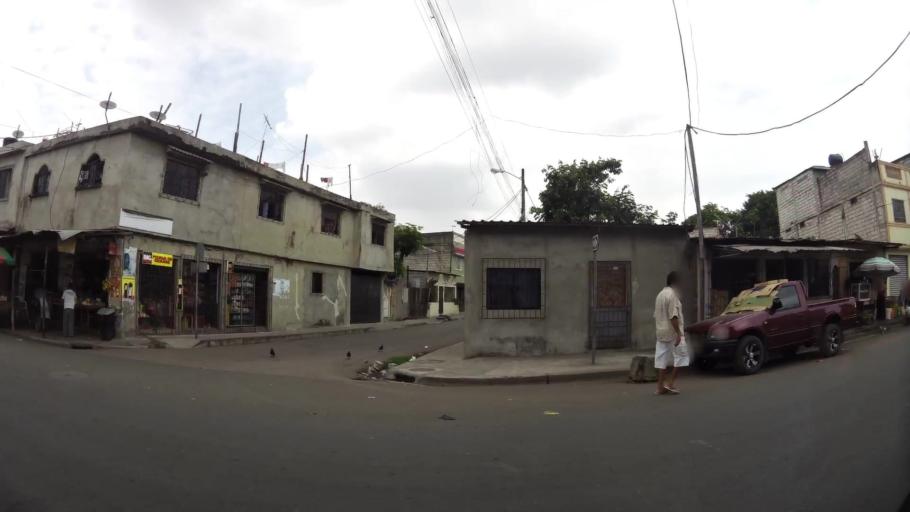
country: EC
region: Guayas
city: Guayaquil
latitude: -2.2305
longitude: -79.9123
